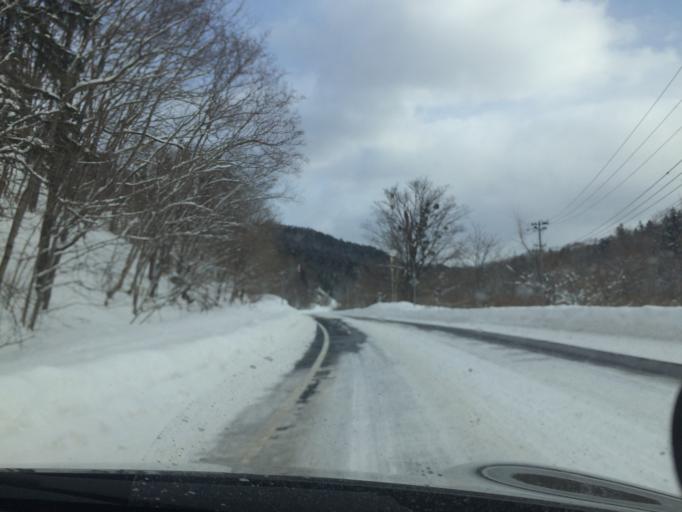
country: JP
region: Hokkaido
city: Shimo-furano
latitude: 43.0498
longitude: 142.5054
